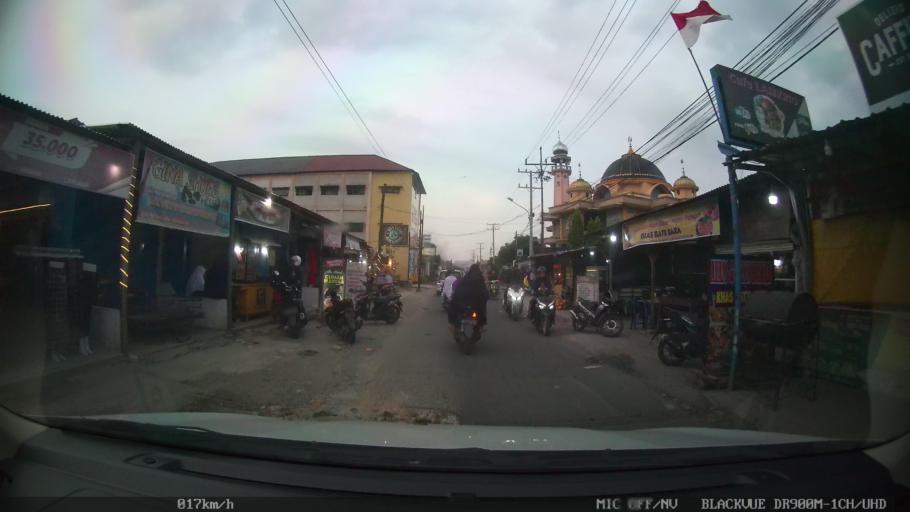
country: ID
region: North Sumatra
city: Sunggal
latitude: 3.5774
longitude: 98.5886
